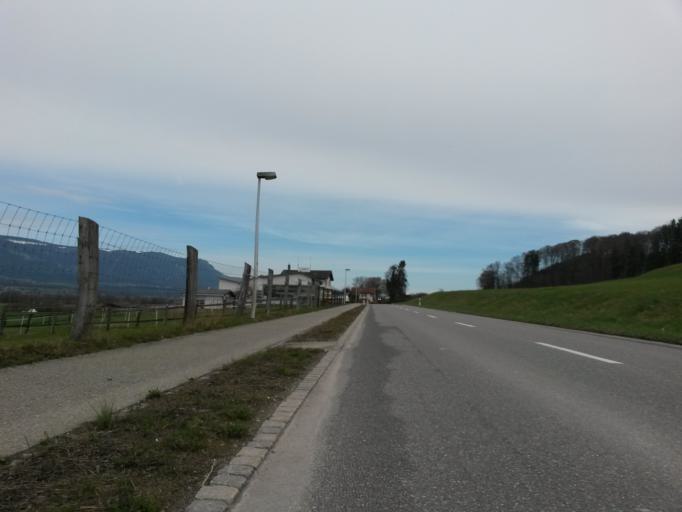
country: CH
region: Bern
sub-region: Seeland District
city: Arch
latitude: 47.1707
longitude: 7.4346
